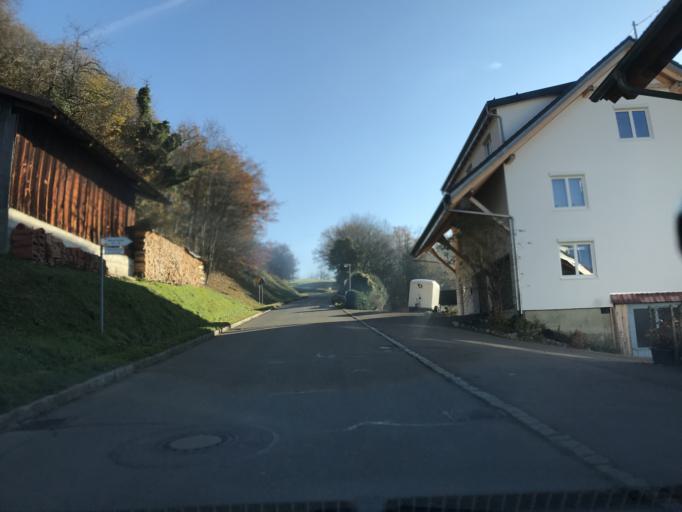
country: DE
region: Baden-Wuerttemberg
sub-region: Freiburg Region
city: Schworstadt
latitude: 47.6154
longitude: 7.8599
